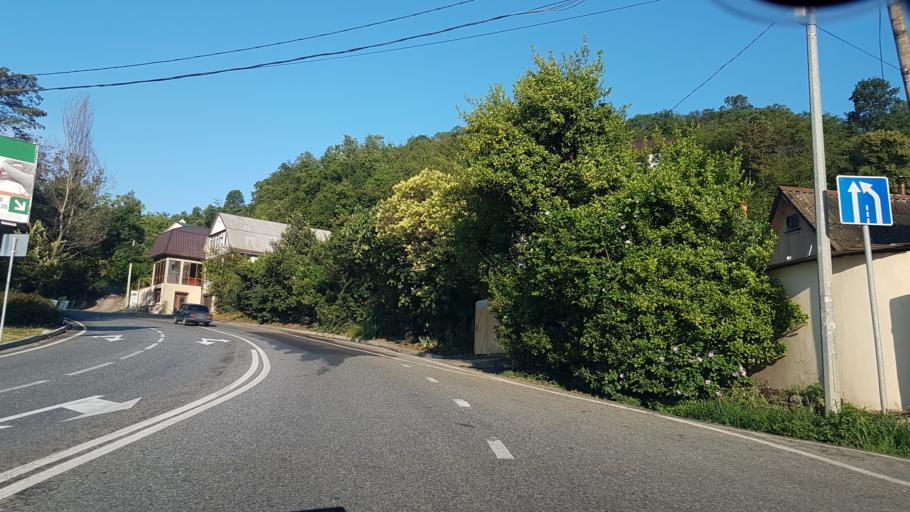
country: RU
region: Krasnodarskiy
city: Dagomys
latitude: 43.6590
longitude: 39.6508
